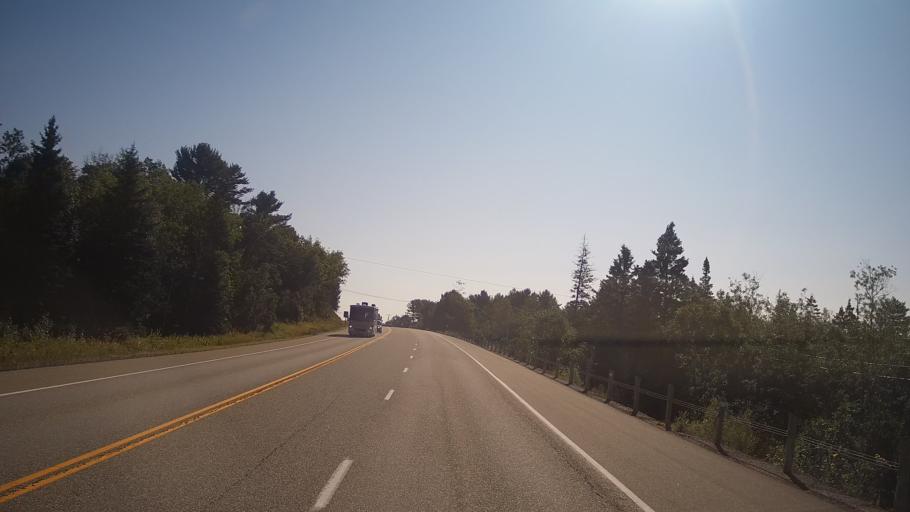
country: CA
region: Ontario
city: Elliot Lake
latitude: 46.2086
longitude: -82.6487
